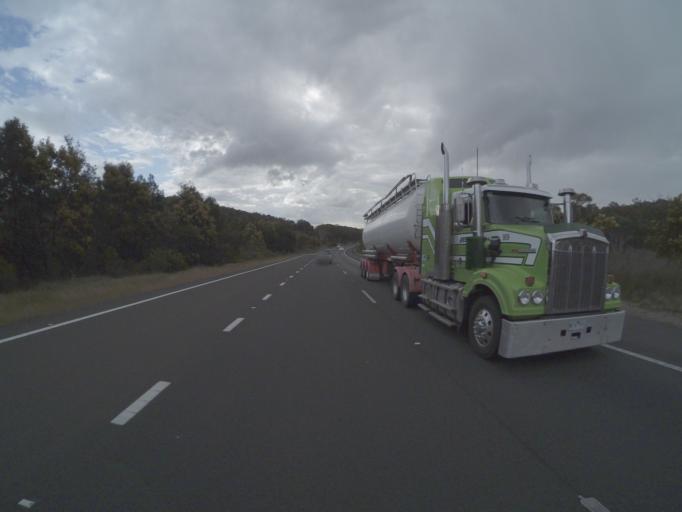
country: AU
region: New South Wales
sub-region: Goulburn Mulwaree
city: Goulburn
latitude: -34.7433
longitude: 149.8432
